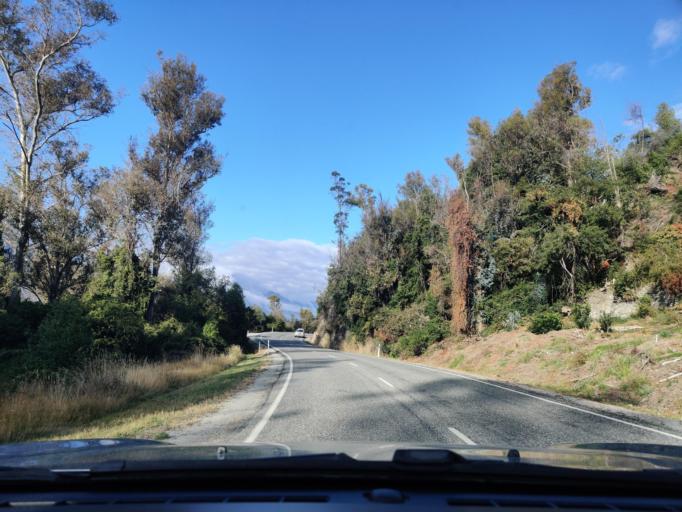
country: NZ
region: Otago
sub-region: Queenstown-Lakes District
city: Queenstown
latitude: -45.0453
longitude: 168.6313
